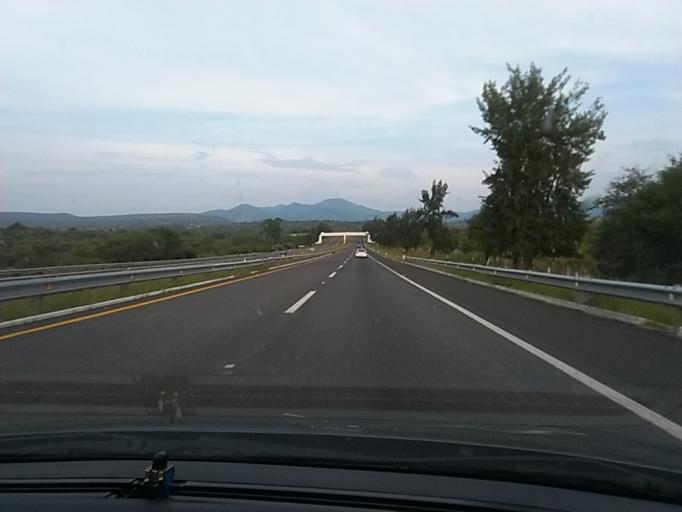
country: MX
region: Michoacan
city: Zinapecuaro
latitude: 19.9009
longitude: -100.8429
